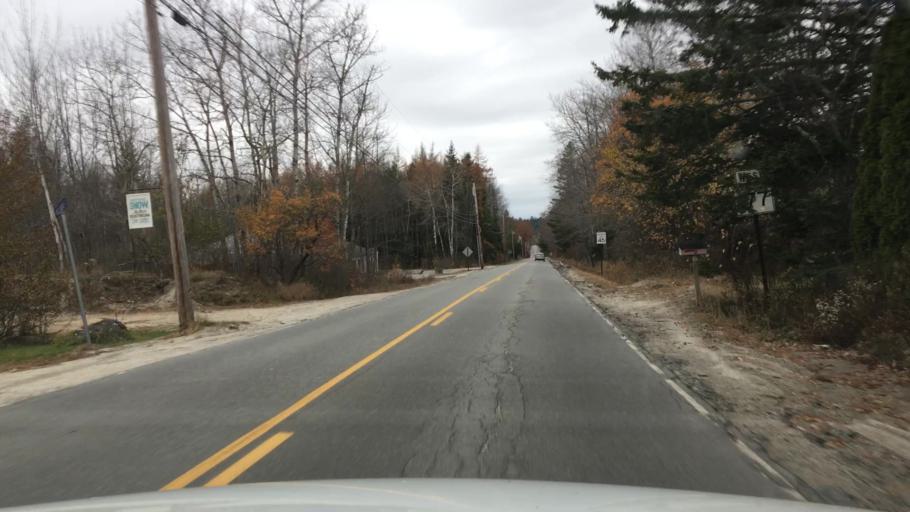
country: US
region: Maine
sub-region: Hancock County
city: Sedgwick
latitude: 44.4148
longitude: -68.6085
